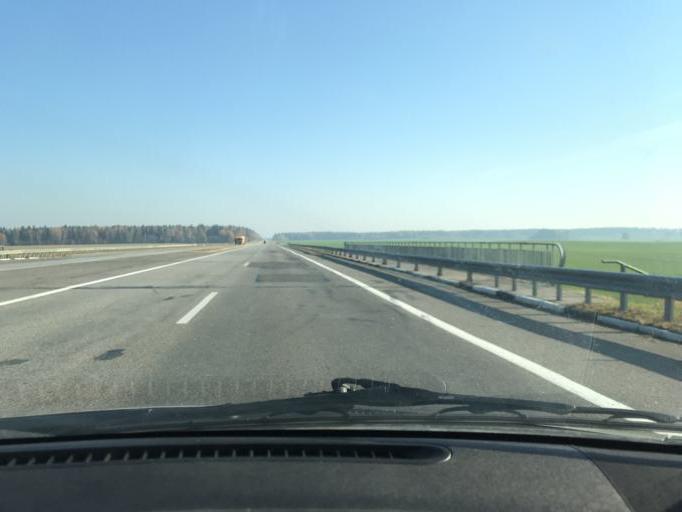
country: BY
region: Vitebsk
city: Talachyn
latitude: 54.4649
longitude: 29.7526
